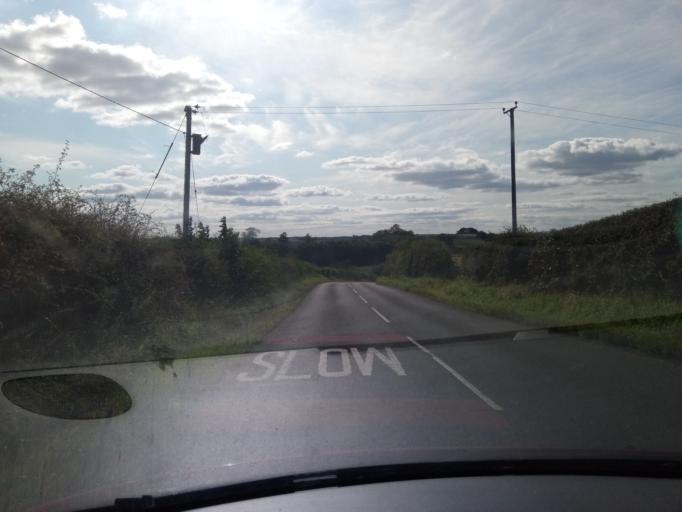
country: GB
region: England
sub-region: Northumberland
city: Berwick-Upon-Tweed
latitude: 55.7668
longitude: -2.0634
